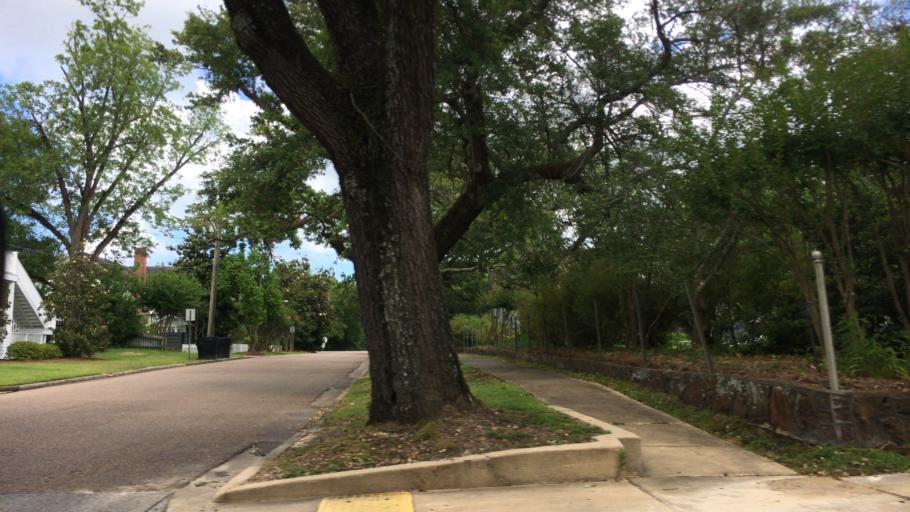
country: US
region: Louisiana
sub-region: Lincoln Parish
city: Ruston
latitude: 32.5344
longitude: -92.6388
